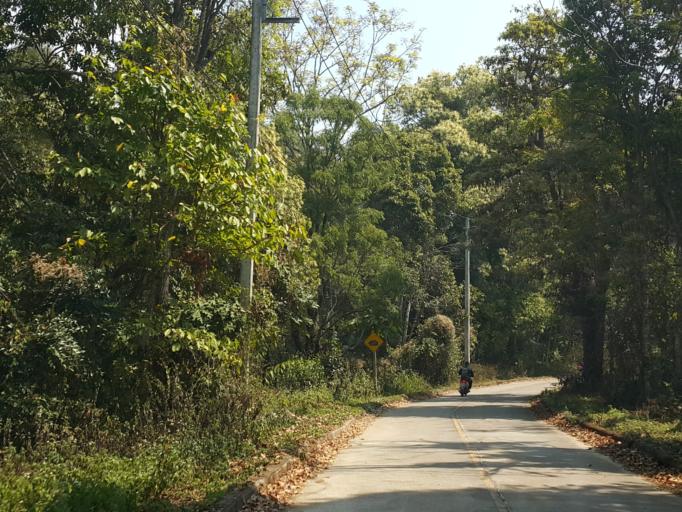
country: TH
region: Lampang
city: Mueang Pan
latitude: 18.8246
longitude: 99.3885
